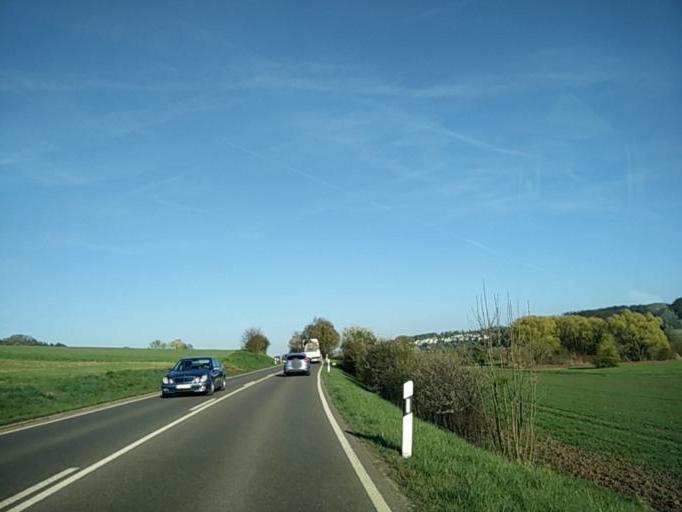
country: DE
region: Baden-Wuerttemberg
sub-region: Tuebingen Region
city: Tuebingen
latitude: 48.5250
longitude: 9.0082
